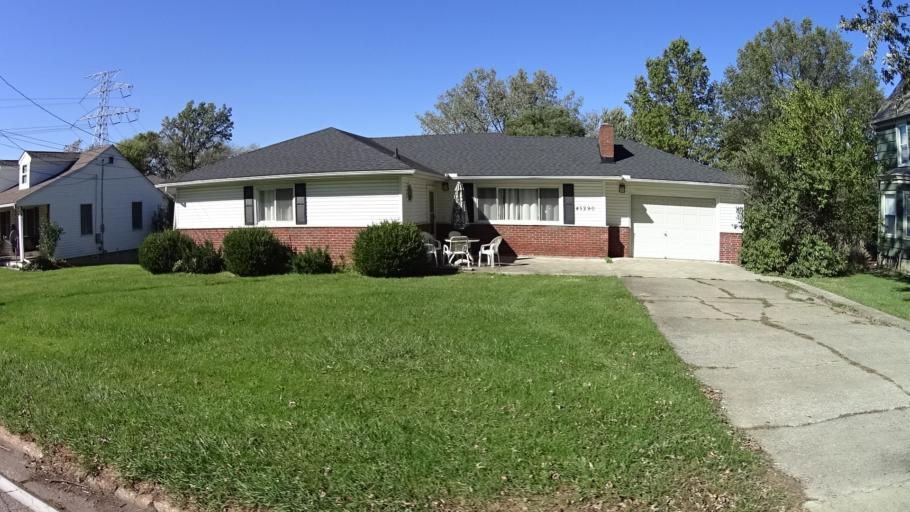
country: US
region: Ohio
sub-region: Lorain County
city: Amherst
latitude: 41.4133
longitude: -82.1923
